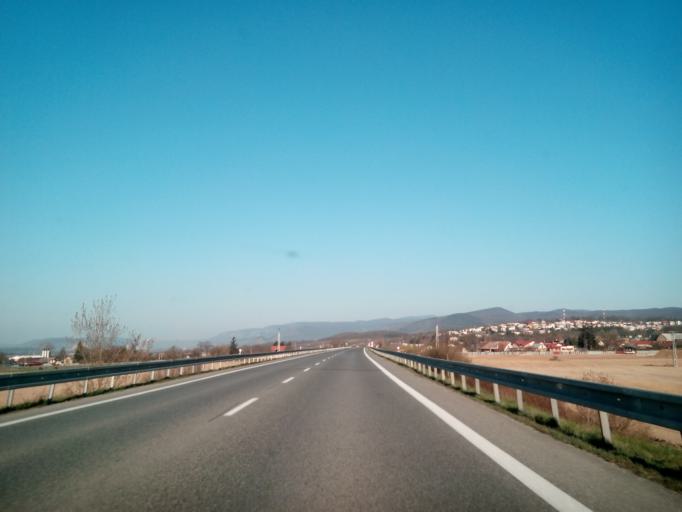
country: SK
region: Kosicky
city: Moldava nad Bodvou
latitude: 48.6049
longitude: 21.0075
